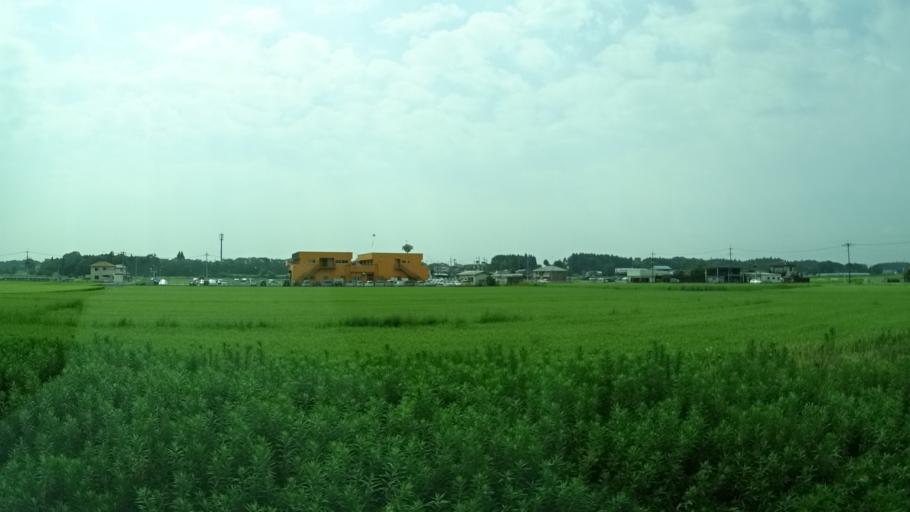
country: JP
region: Tochigi
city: Mashiko
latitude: 36.4935
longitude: 140.0946
